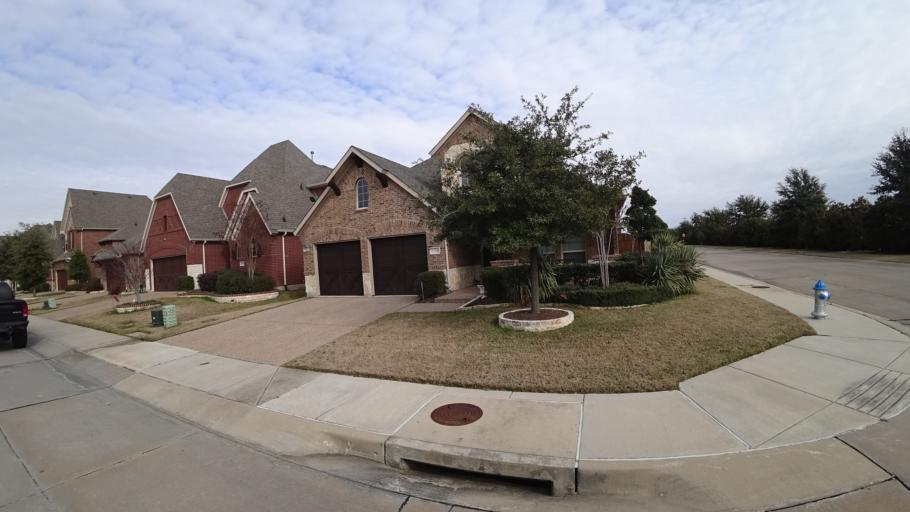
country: US
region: Texas
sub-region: Denton County
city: The Colony
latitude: 33.0514
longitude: -96.9087
